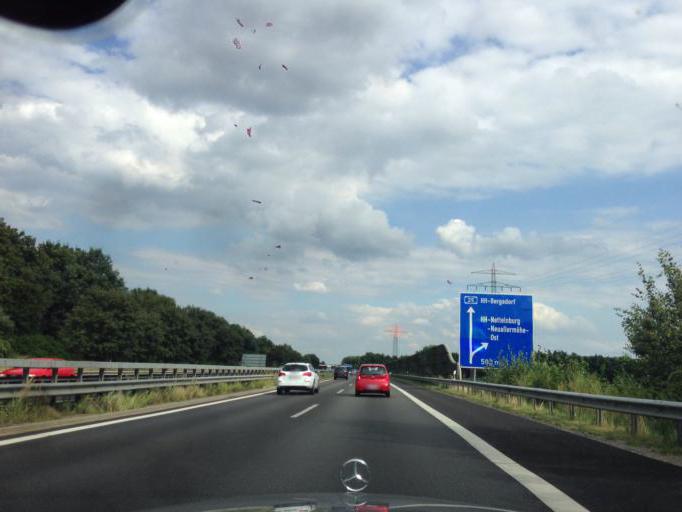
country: DE
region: Hamburg
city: Bergedorf
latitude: 53.4758
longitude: 10.1660
